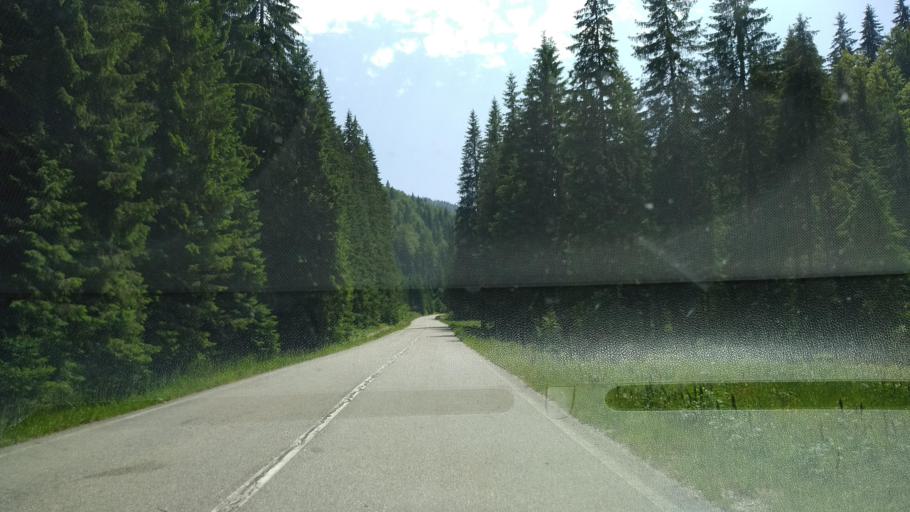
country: RO
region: Gorj
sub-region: Comuna Pades
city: Closani
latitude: 45.2618
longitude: 22.8707
